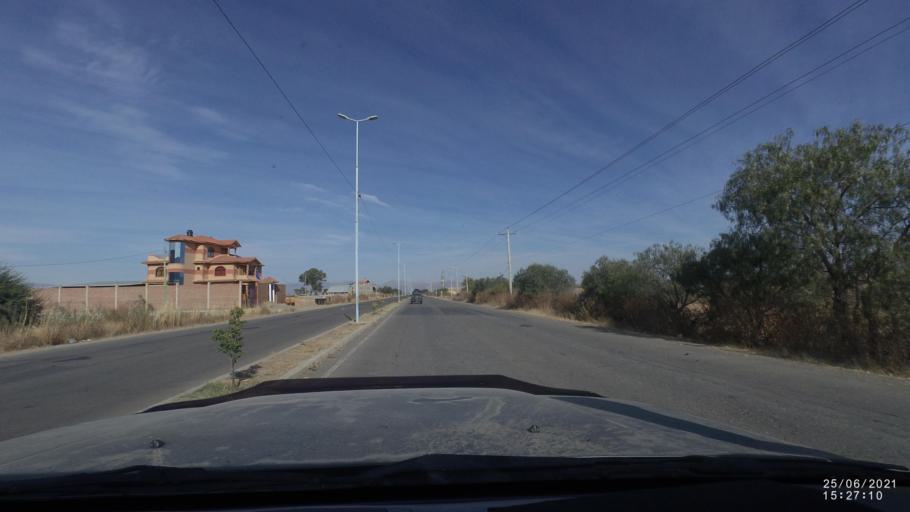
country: BO
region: Cochabamba
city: Cliza
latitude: -17.5467
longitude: -65.9522
